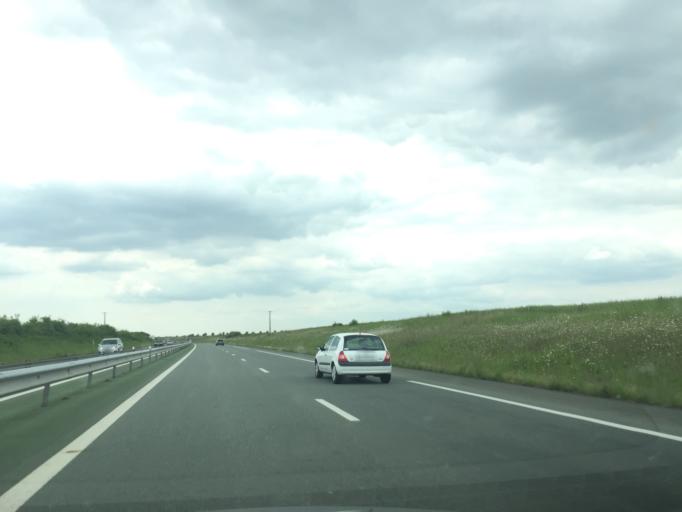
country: FR
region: Poitou-Charentes
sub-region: Departement des Deux-Sevres
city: Villiers-en-Plaine
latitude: 46.4275
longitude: -0.5319
